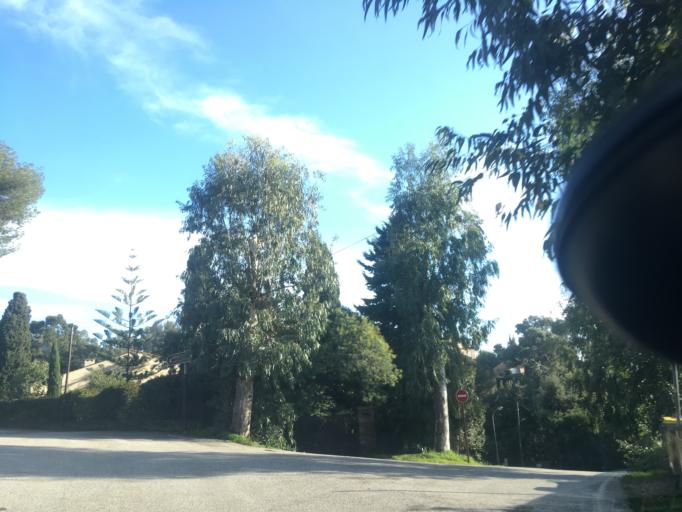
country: FR
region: Provence-Alpes-Cote d'Azur
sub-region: Departement du Var
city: Cavalaire-sur-Mer
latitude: 43.1570
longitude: 6.4792
